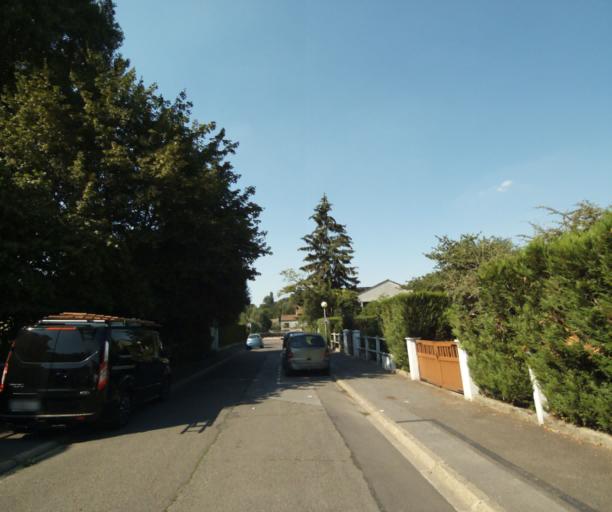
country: FR
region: Ile-de-France
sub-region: Departement de Seine-et-Marne
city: Pomponne
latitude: 48.8791
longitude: 2.6977
